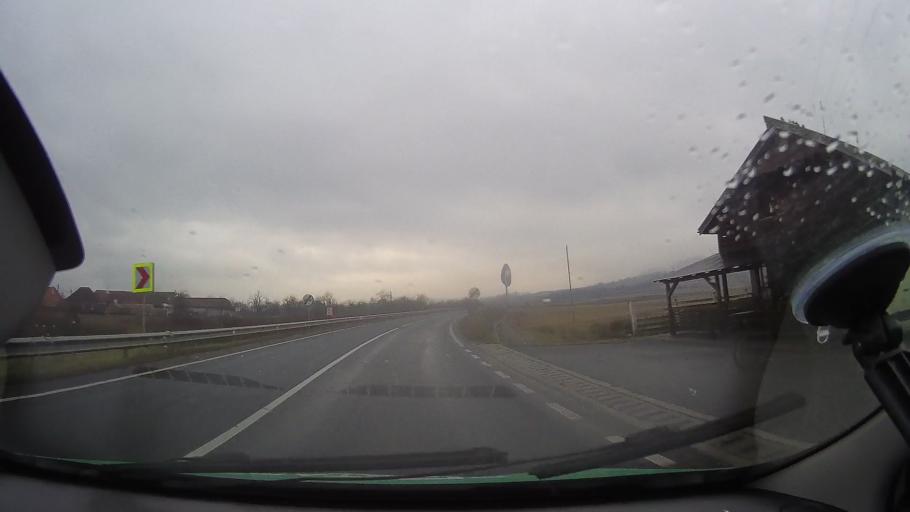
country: RO
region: Hunedoara
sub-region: Comuna Baia de Cris
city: Baia de Cris
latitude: 46.1777
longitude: 22.7064
